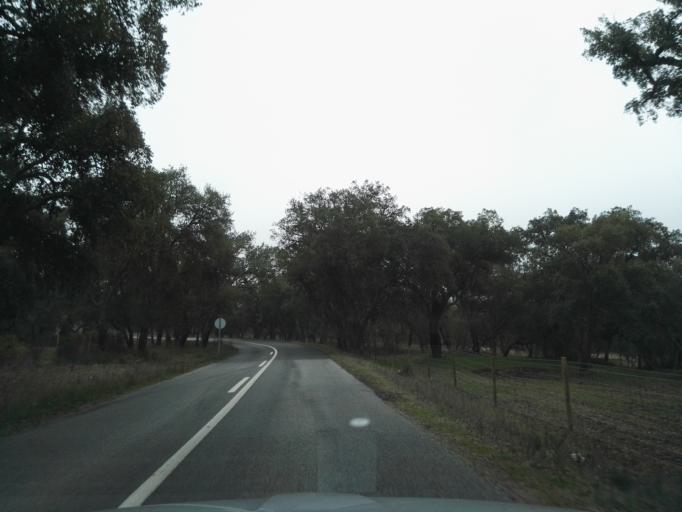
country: PT
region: Evora
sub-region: Vendas Novas
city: Vendas Novas
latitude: 38.7674
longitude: -8.3800
